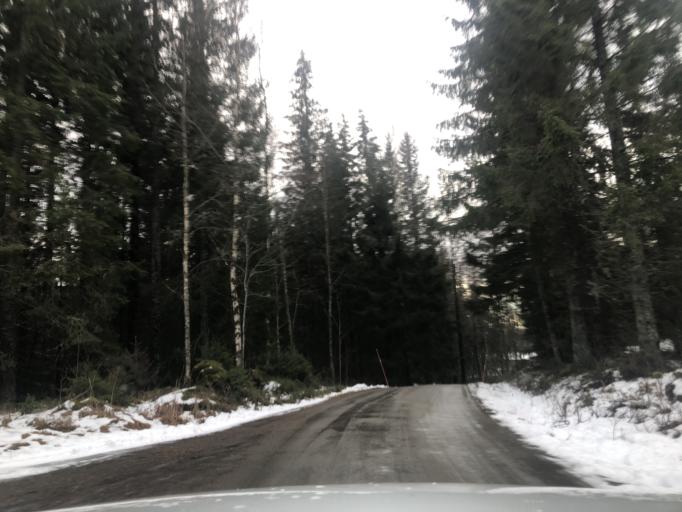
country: SE
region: Vaestra Goetaland
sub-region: Ulricehamns Kommun
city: Ulricehamn
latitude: 57.7737
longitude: 13.4734
